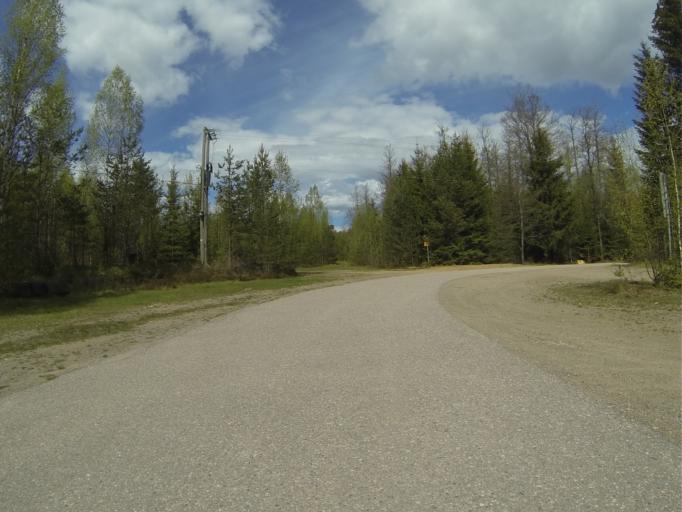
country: FI
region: Varsinais-Suomi
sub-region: Salo
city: Halikko
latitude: 60.3019
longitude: 23.0764
